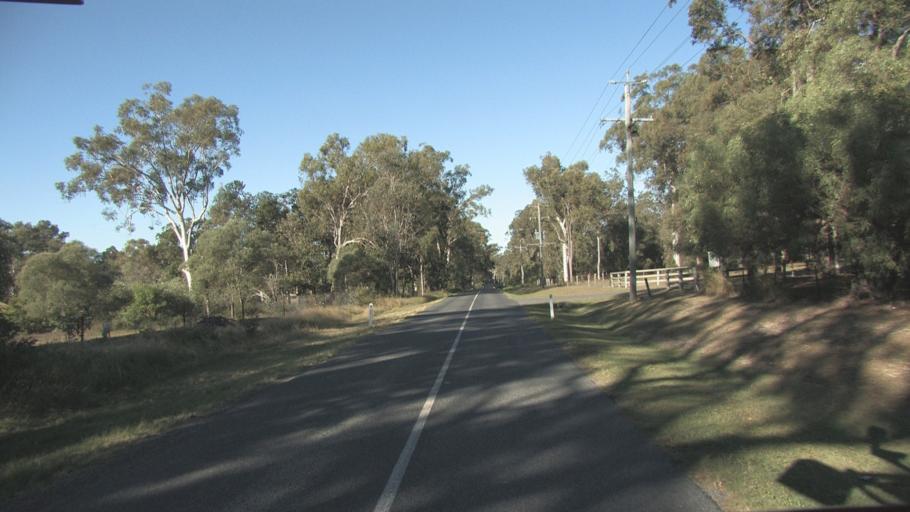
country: AU
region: Queensland
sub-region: Logan
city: Logan Reserve
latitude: -27.7398
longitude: 153.0953
